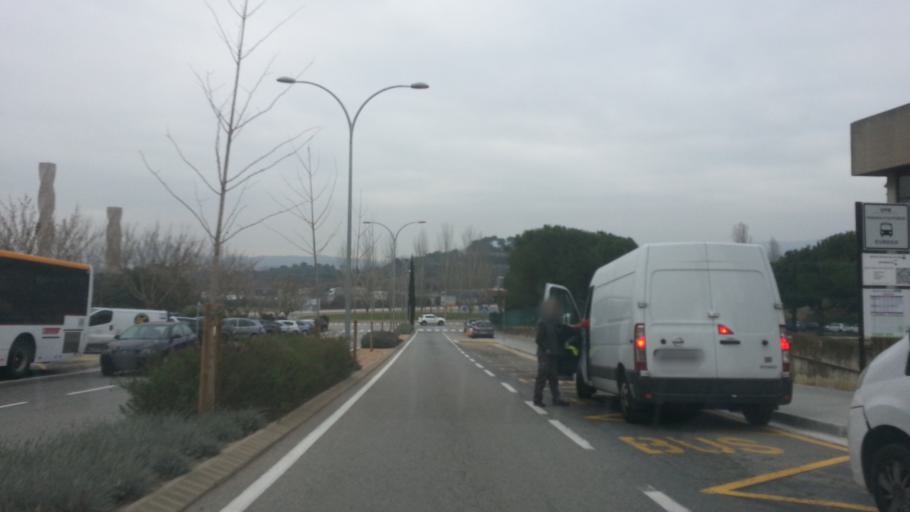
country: ES
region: Catalonia
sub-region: Provincia de Barcelona
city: Barbera del Valles
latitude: 41.4968
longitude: 2.1080
